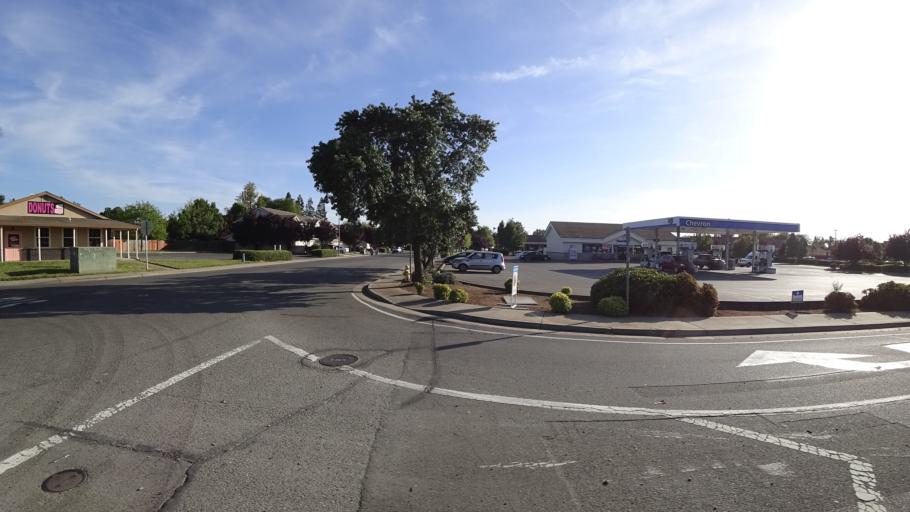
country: US
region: California
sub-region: Yuba County
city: Wheatland
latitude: 39.0144
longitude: -121.4312
